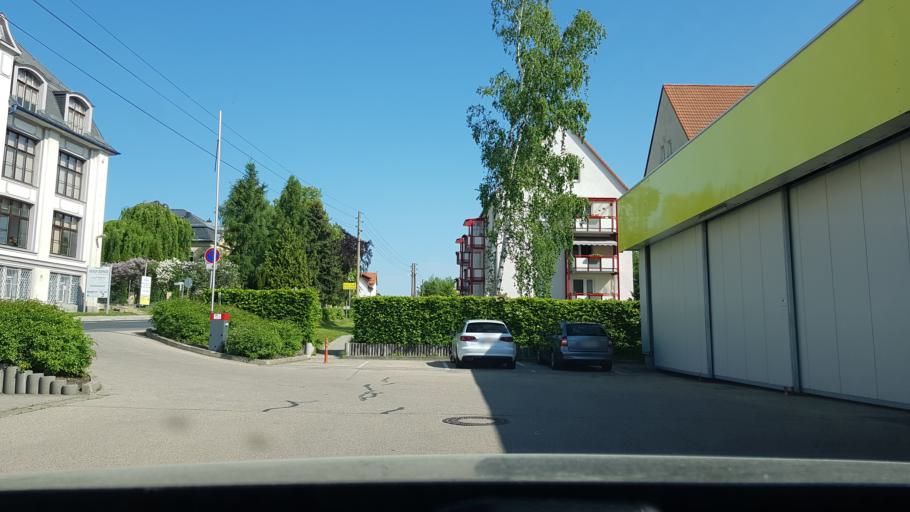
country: DE
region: Saxony
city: Wittgensdorf
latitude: 50.8753
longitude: 12.8711
